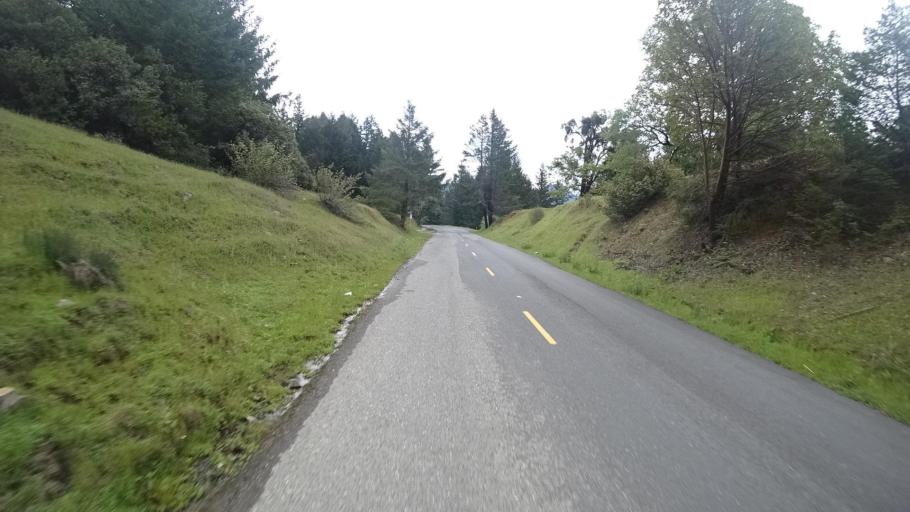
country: US
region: California
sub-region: Humboldt County
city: Redway
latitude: 40.1209
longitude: -123.6470
